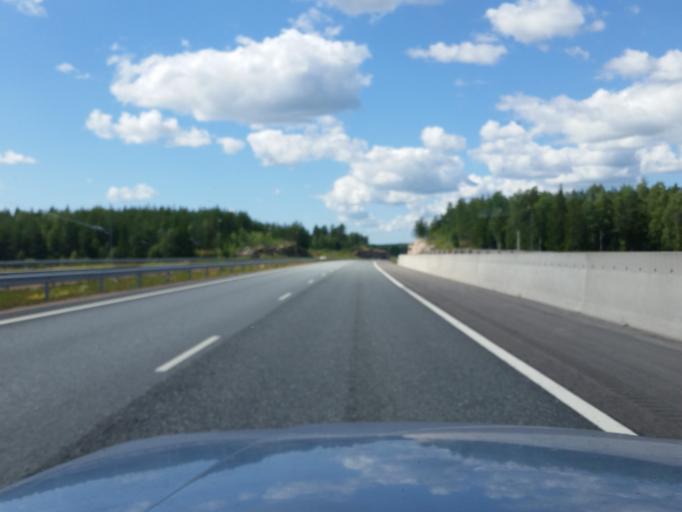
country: FI
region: Varsinais-Suomi
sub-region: Salo
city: Suomusjaervi
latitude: 60.3709
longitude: 23.7059
